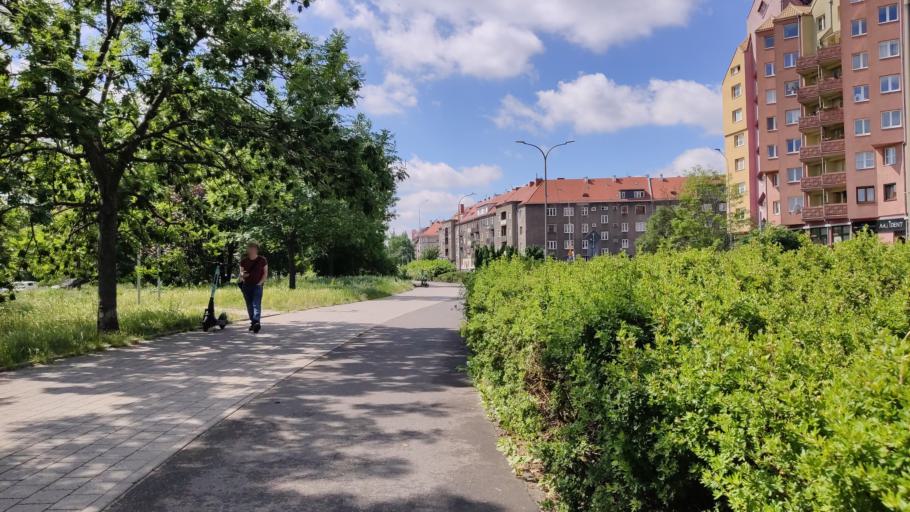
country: PL
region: Lower Silesian Voivodeship
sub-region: Powiat wroclawski
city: Wroclaw
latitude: 51.1282
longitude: 17.0556
